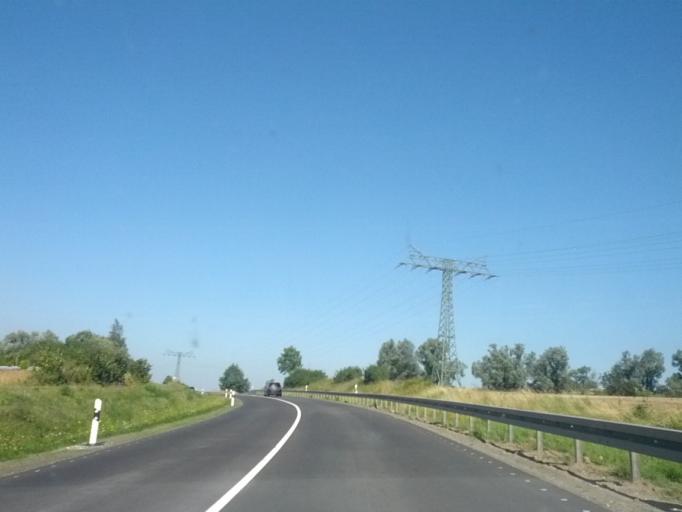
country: DE
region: Mecklenburg-Vorpommern
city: Sagard
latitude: 54.5000
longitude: 13.5627
